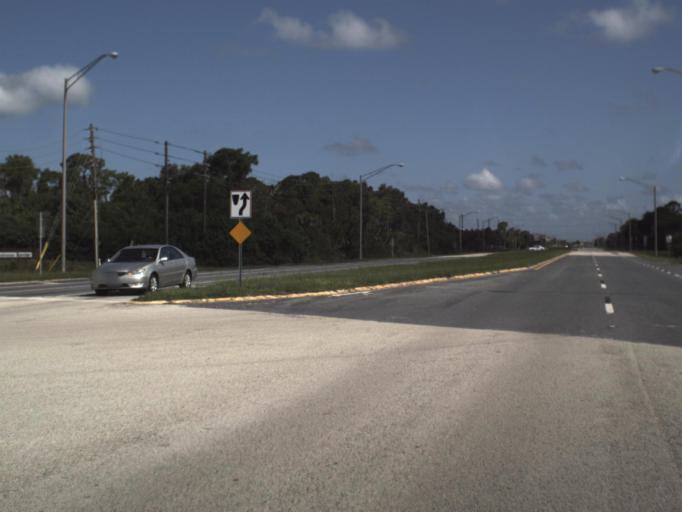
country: US
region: Florida
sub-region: Pinellas County
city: Gandy
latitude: 27.8700
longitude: -82.6469
